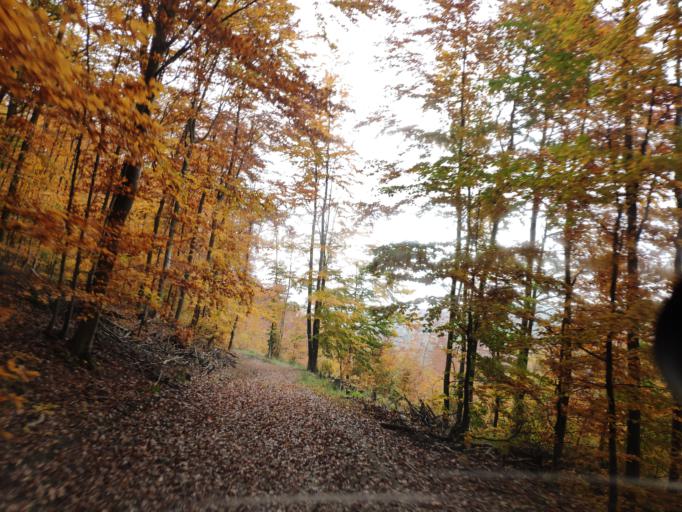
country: SK
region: Kosicky
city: Moldava nad Bodvou
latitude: 48.7354
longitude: 21.0251
